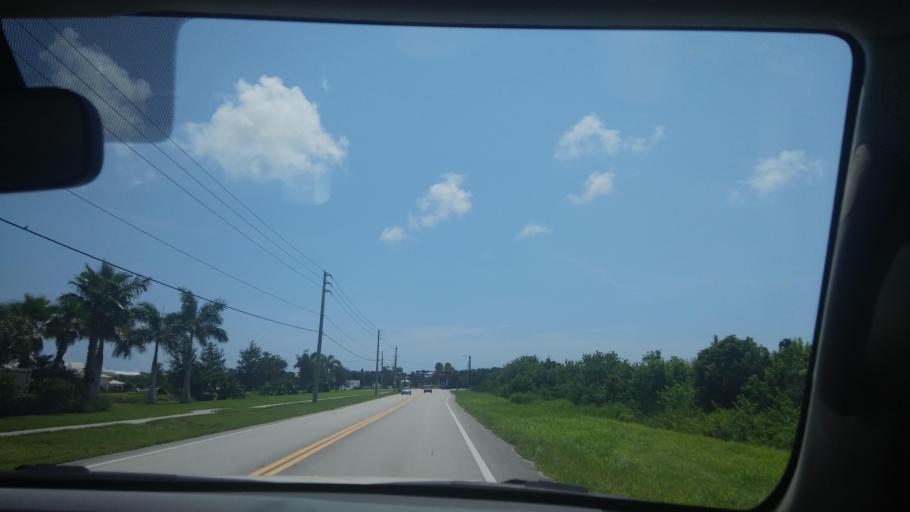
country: US
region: Florida
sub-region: Indian River County
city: Gifford
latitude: 27.6676
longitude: -80.3965
